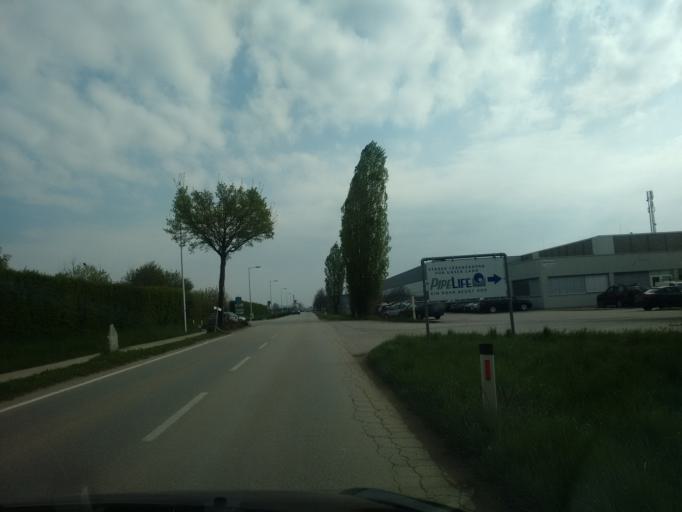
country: AT
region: Upper Austria
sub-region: Wels-Land
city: Gunskirchen
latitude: 48.1436
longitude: 13.9666
